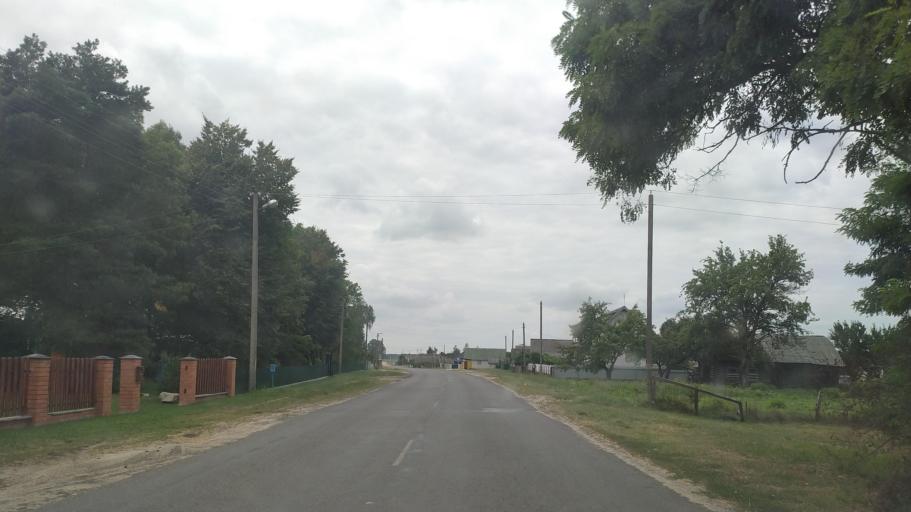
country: BY
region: Brest
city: Byaroza
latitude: 52.5421
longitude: 25.0739
